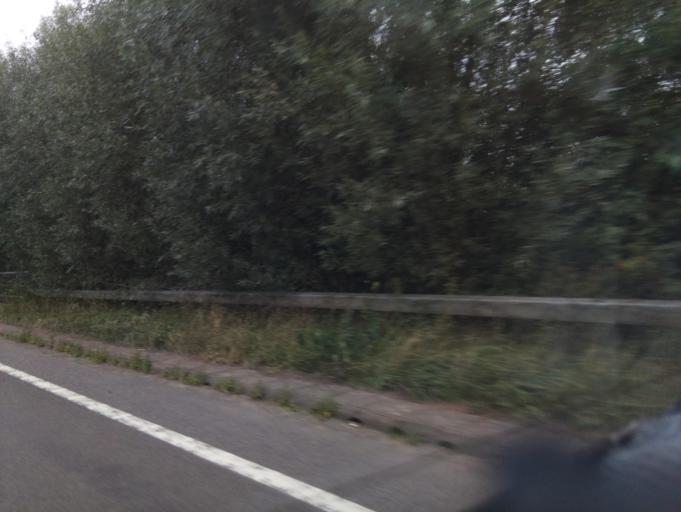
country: GB
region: England
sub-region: Shropshire
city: Stoke upon Tern
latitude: 52.8633
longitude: -2.5555
